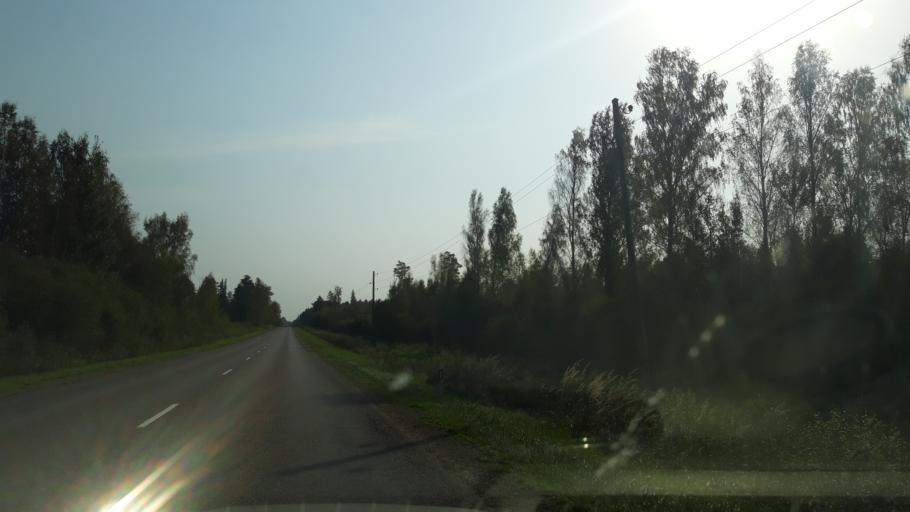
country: LV
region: Burtnieki
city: Matisi
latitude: 57.6482
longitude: 25.2399
